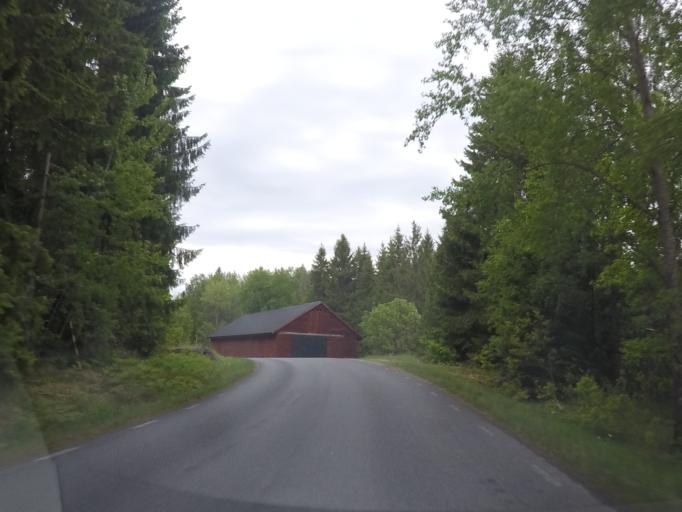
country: SE
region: Soedermanland
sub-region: Eskilstuna Kommun
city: Arla
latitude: 59.2604
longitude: 16.6541
